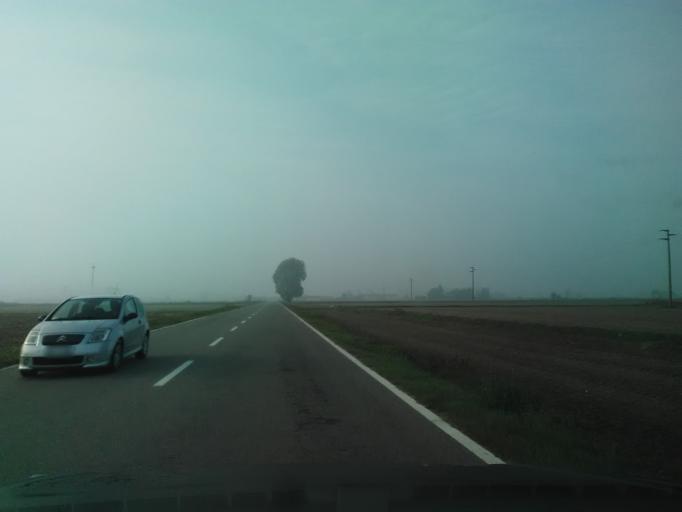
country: IT
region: Piedmont
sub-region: Provincia di Vercelli
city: Tronzano Vercellese
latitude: 45.3535
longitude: 8.1702
